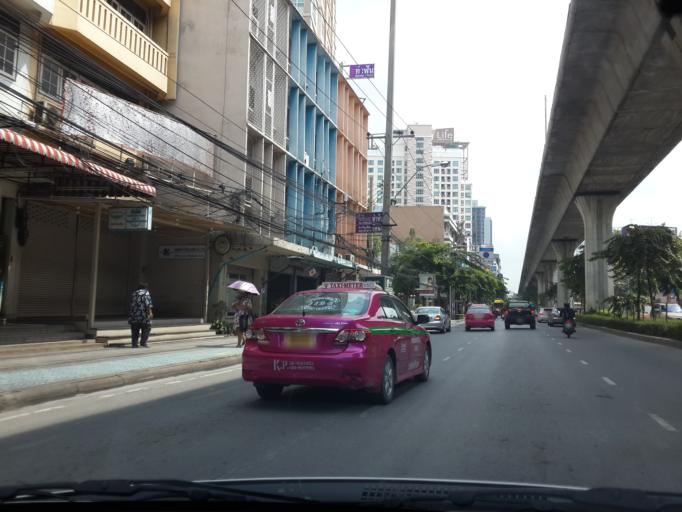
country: TH
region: Bangkok
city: Phaya Thai
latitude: 13.7871
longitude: 100.5473
